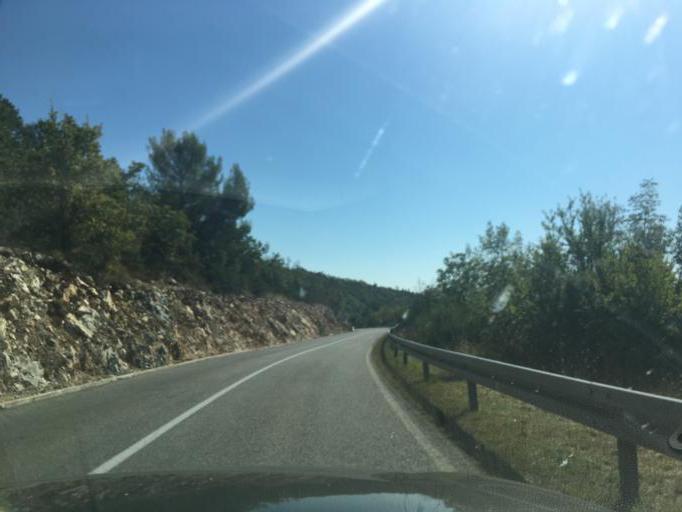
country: HR
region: Splitsko-Dalmatinska
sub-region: Grad Trogir
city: Trogir
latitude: 43.5758
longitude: 16.2342
